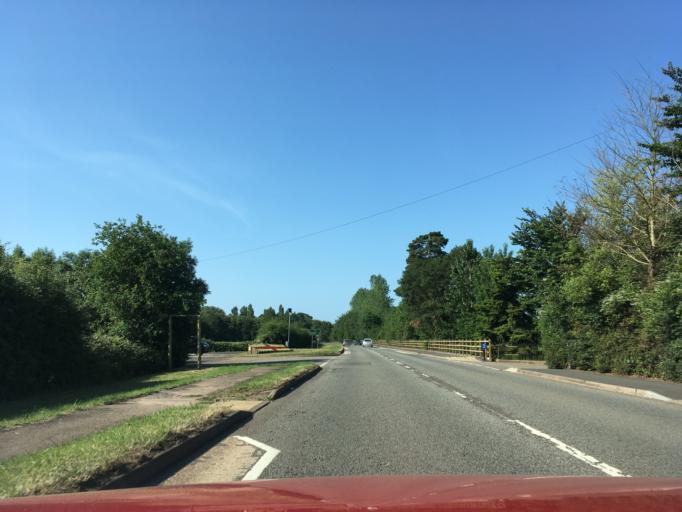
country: GB
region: England
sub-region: Gloucestershire
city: Lydney
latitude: 51.7207
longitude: -2.5419
